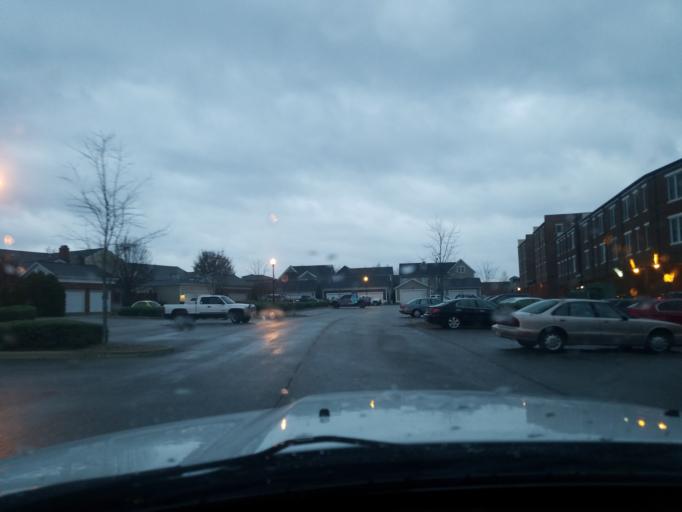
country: US
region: Kentucky
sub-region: Jefferson County
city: Worthington
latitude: 38.3243
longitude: -85.5653
